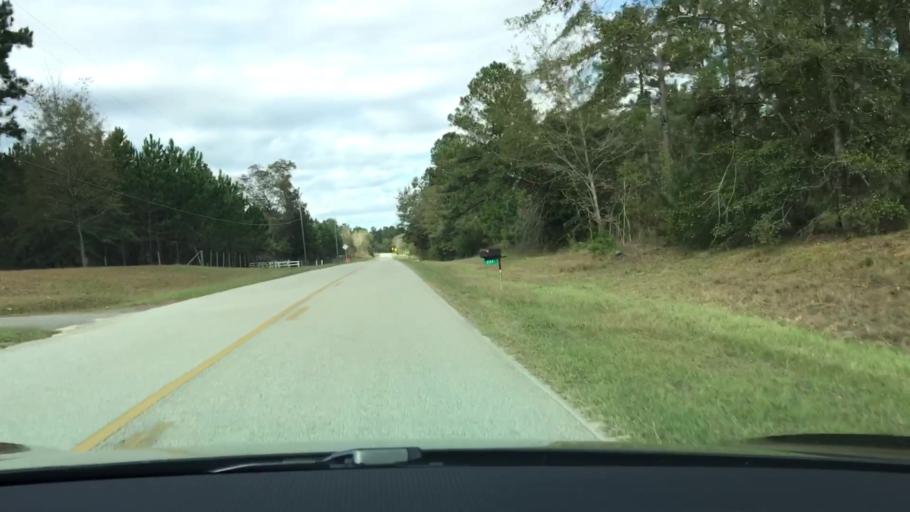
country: US
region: Georgia
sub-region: Jefferson County
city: Wadley
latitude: 32.7993
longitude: -82.3798
